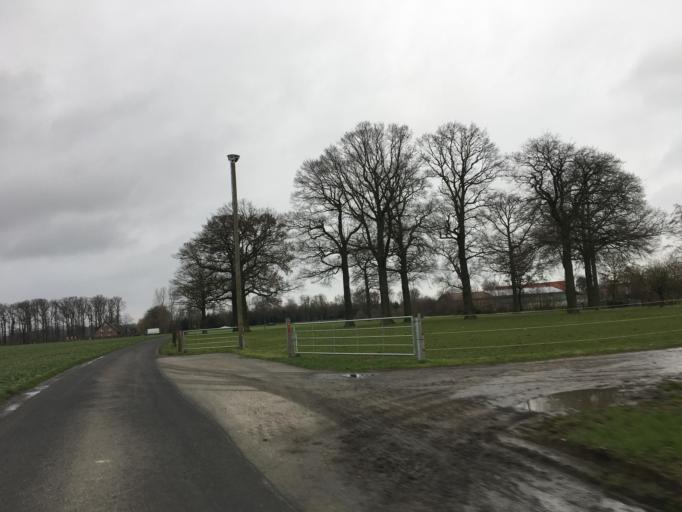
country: DE
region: North Rhine-Westphalia
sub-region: Regierungsbezirk Munster
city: Senden
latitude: 51.8758
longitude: 7.4509
